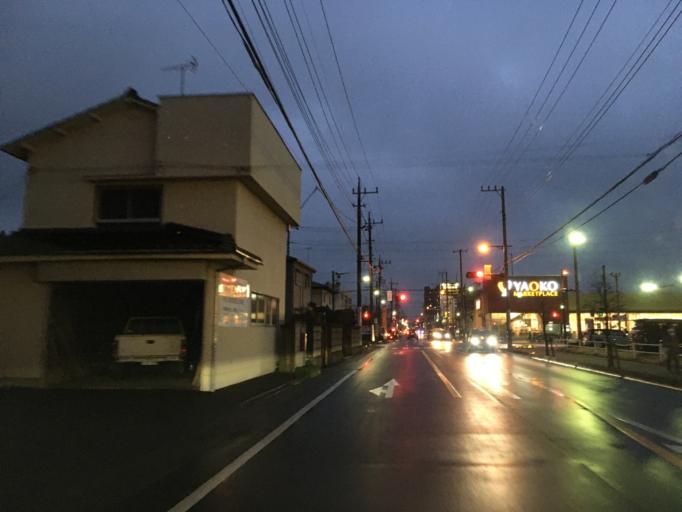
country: JP
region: Saitama
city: Asaka
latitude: 35.7997
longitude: 139.5685
